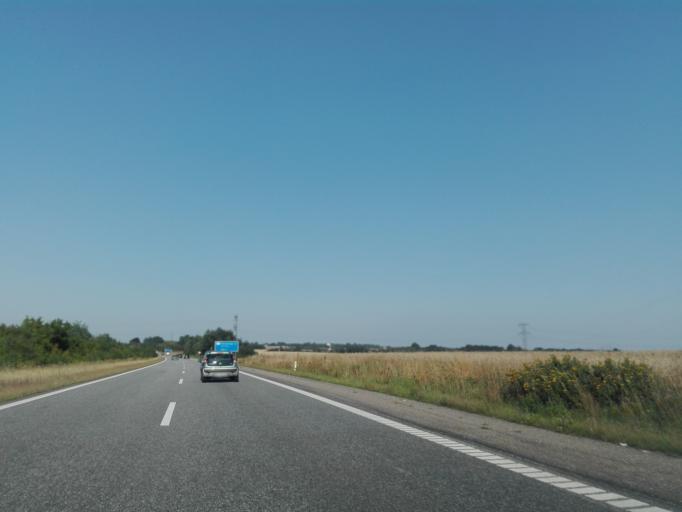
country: DK
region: Central Jutland
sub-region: Skanderborg Kommune
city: Horning
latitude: 56.1019
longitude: 10.0398
